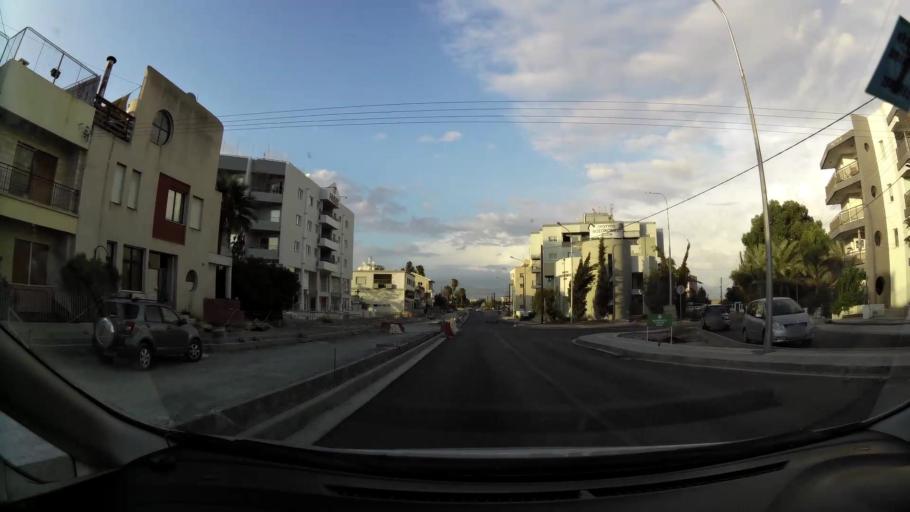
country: CY
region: Lefkosia
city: Nicosia
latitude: 35.1578
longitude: 33.3973
